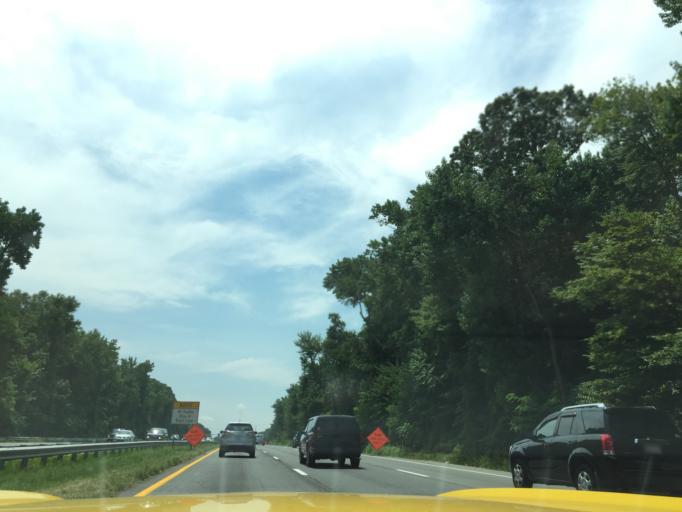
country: US
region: Maryland
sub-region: Prince George's County
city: Fort Washington
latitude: 38.7164
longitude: -76.9900
